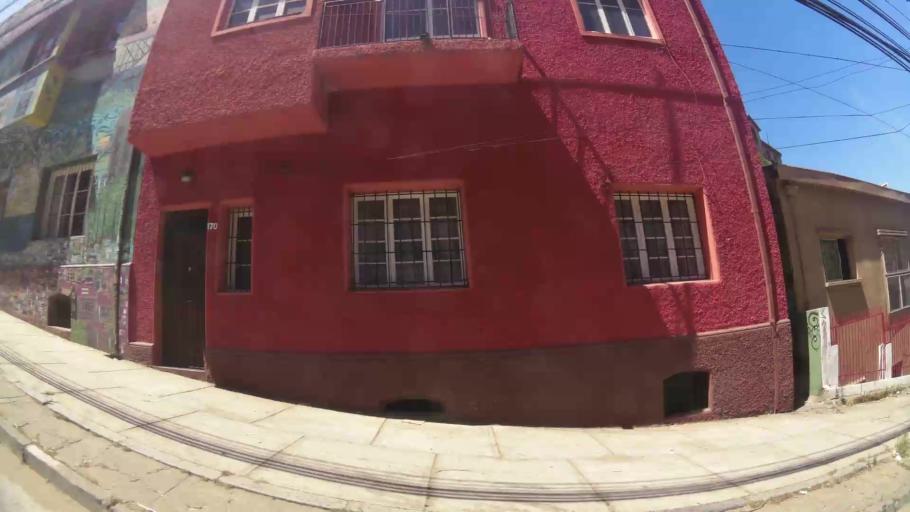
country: CL
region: Valparaiso
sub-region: Provincia de Valparaiso
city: Valparaiso
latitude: -33.0336
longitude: -71.6322
